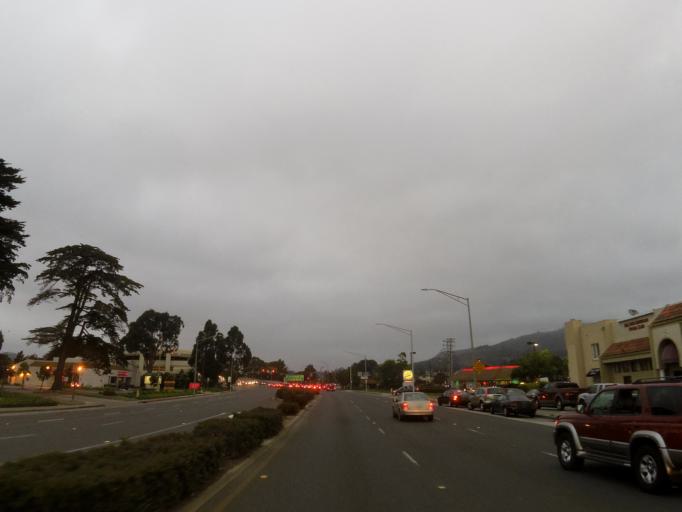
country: US
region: California
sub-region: San Mateo County
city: South San Francisco
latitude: 37.6534
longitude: -122.4325
